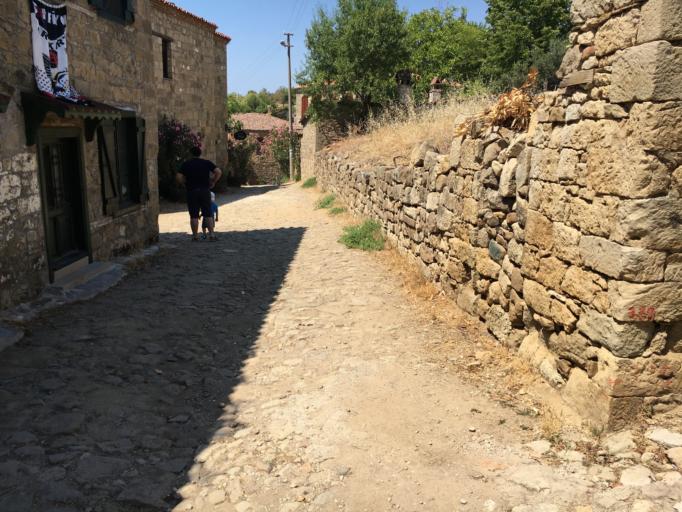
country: TR
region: Canakkale
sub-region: Merkez
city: Kucukkuyu
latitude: 39.5704
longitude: 26.6196
